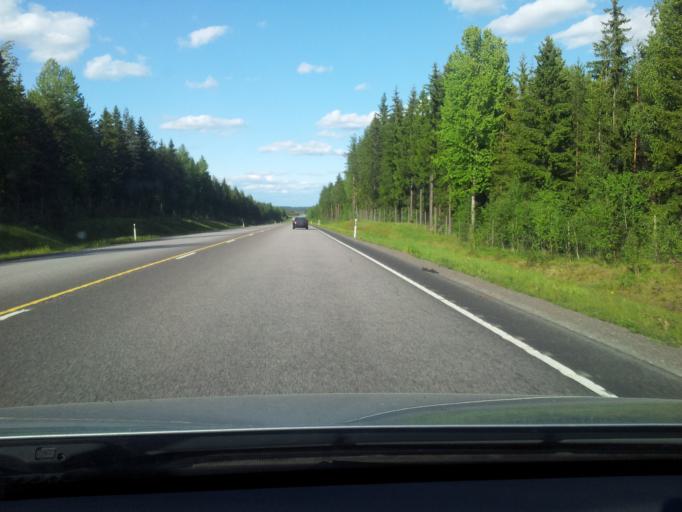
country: FI
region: Uusimaa
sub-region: Loviisa
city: Lapinjaervi
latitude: 60.6866
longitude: 26.2702
